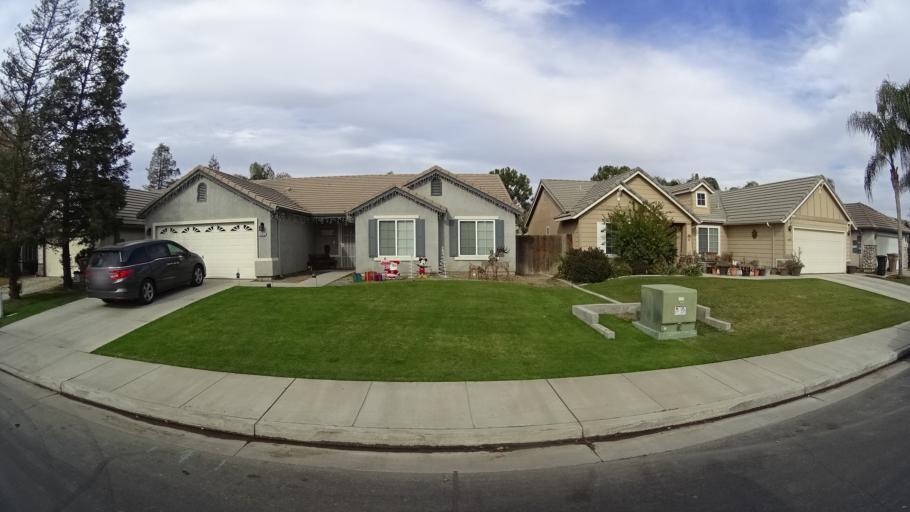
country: US
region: California
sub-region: Kern County
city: Rosedale
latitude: 35.4174
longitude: -119.1424
